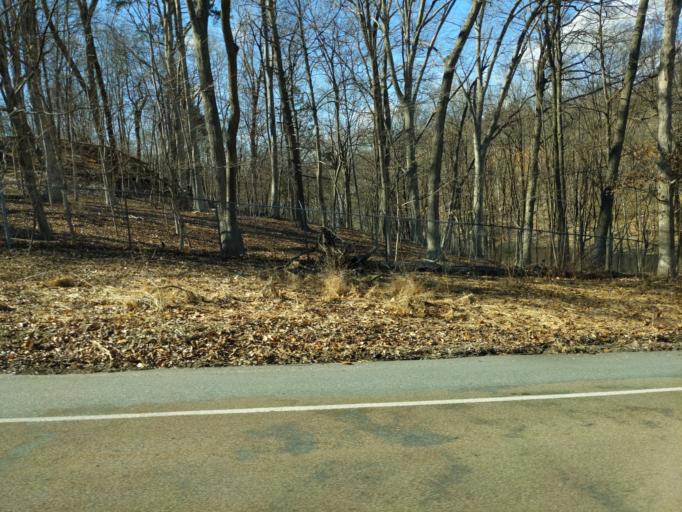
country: US
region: Pennsylvania
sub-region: Montgomery County
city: Red Hill
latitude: 40.3390
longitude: -75.4761
